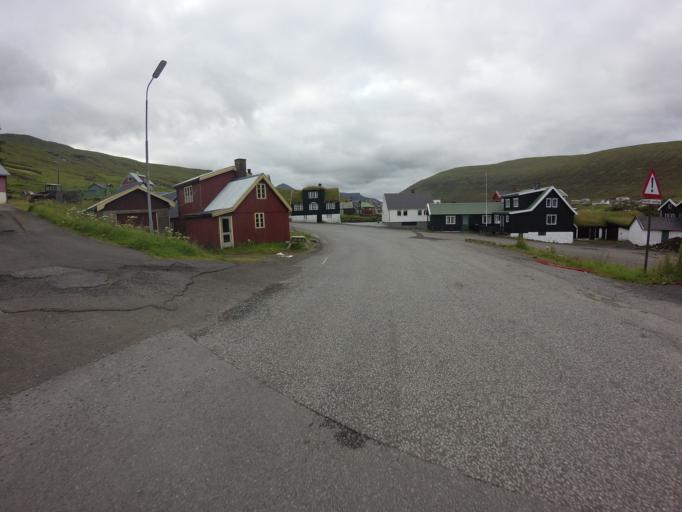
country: FO
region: Eysturoy
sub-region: Eidi
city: Eidi
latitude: 62.1870
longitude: -7.0361
